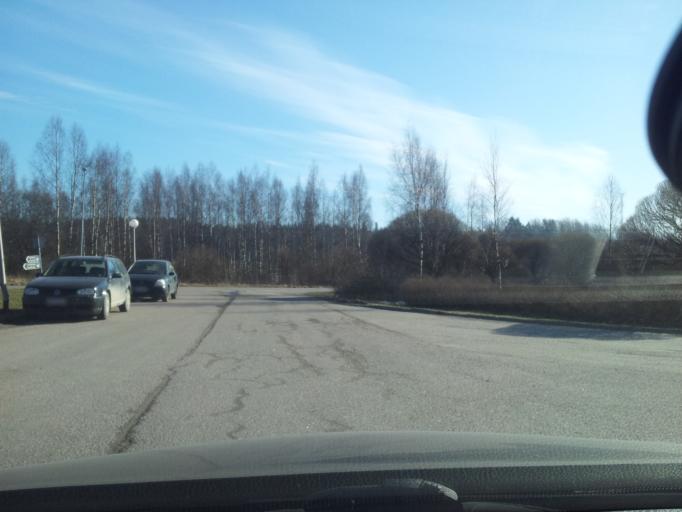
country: FI
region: Uusimaa
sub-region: Helsinki
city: Kirkkonummi
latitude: 60.1530
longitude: 24.5367
